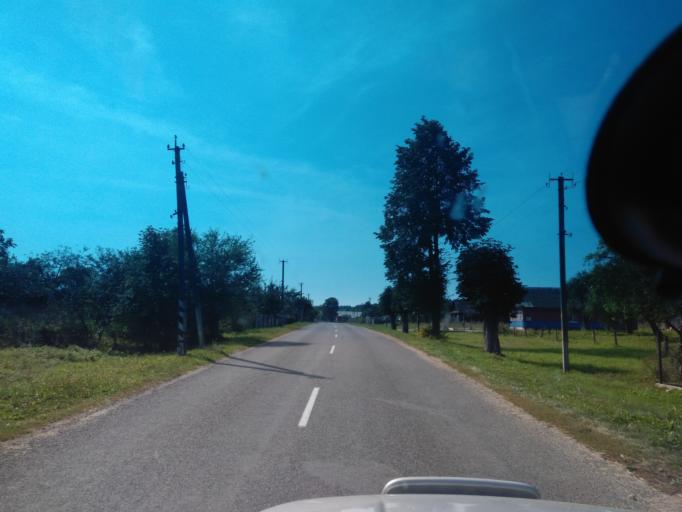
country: BY
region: Minsk
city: Kapyl'
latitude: 53.2042
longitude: 27.1191
